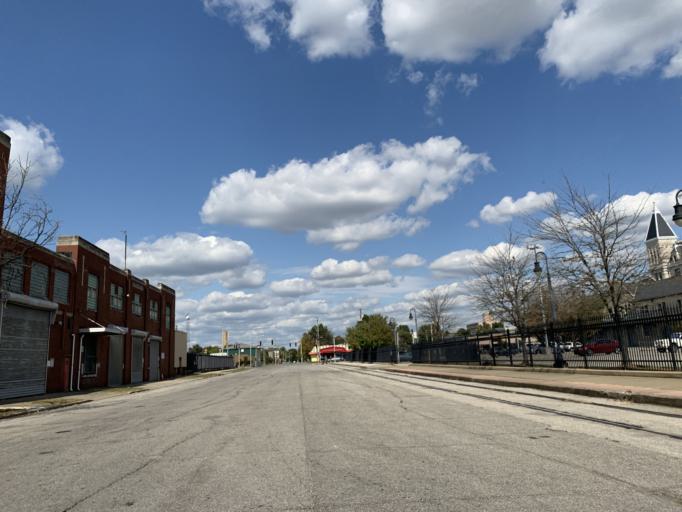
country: US
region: Kentucky
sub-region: Jefferson County
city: Louisville
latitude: 38.2460
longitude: -85.7701
